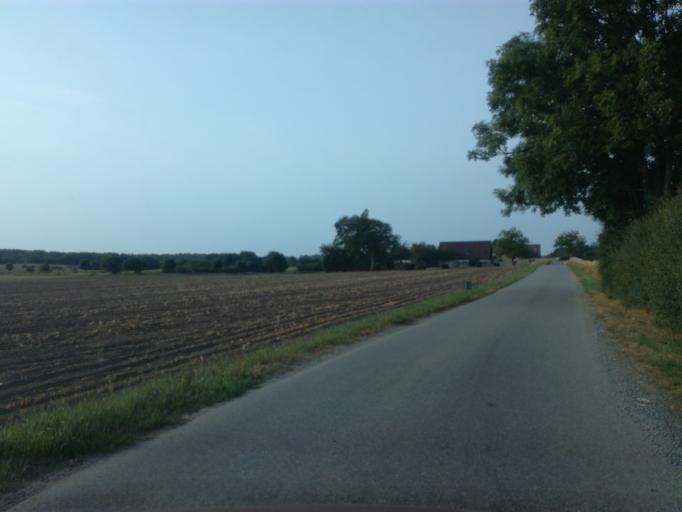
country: DK
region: South Denmark
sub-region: Vejle Kommune
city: Borkop
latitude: 55.6398
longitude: 9.6147
